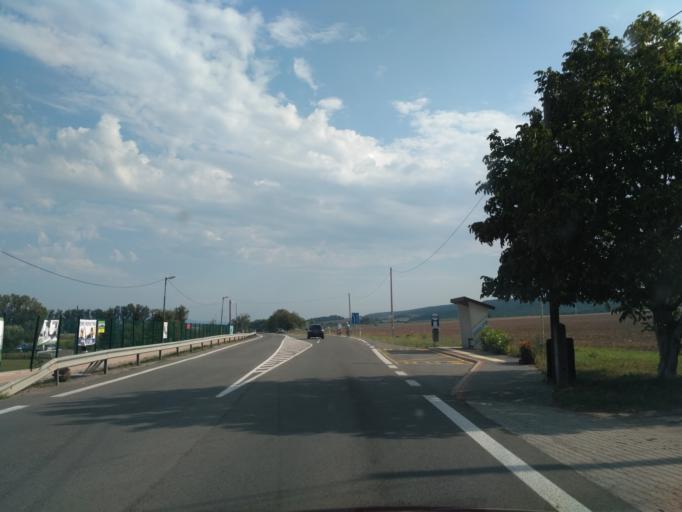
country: SK
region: Kosicky
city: Kosice
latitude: 48.7950
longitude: 21.3057
